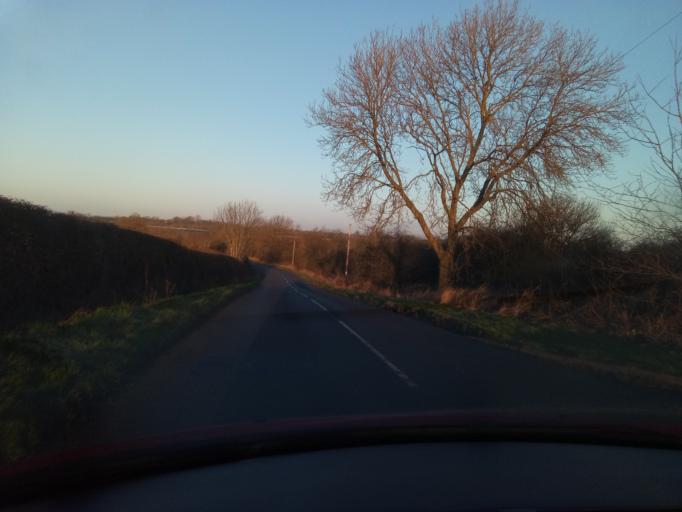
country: GB
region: England
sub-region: Leicestershire
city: Sileby
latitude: 52.7627
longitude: -1.1050
